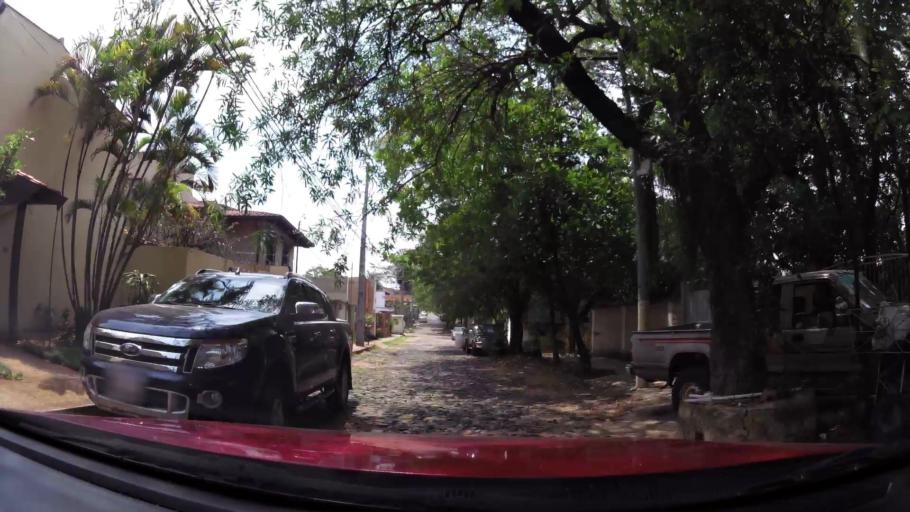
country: PY
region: Asuncion
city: Asuncion
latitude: -25.2716
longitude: -57.5942
